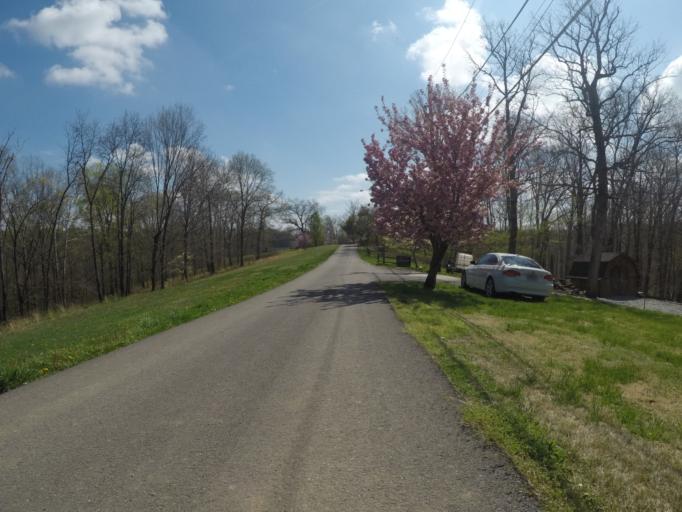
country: US
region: Ohio
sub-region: Lawrence County
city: Burlington
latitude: 38.3906
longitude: -82.5347
